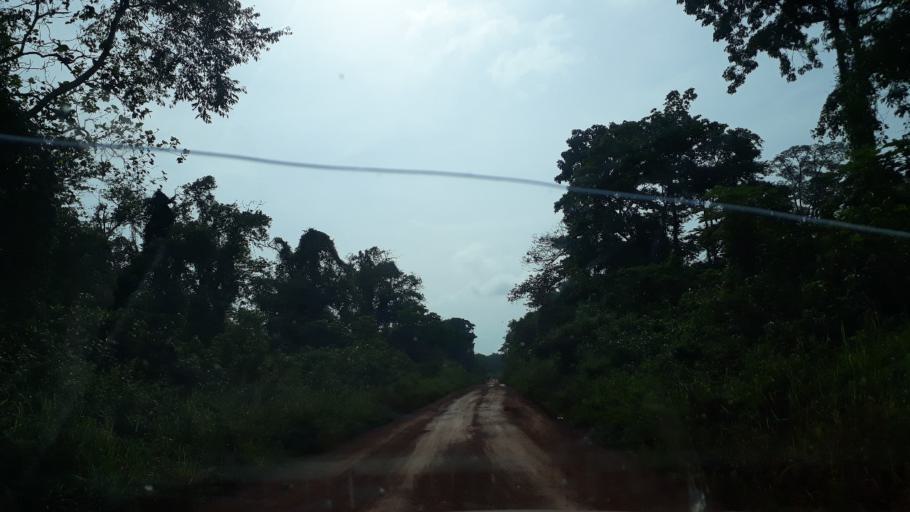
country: CD
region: Eastern Province
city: Wamba
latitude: 1.4069
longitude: 27.6441
